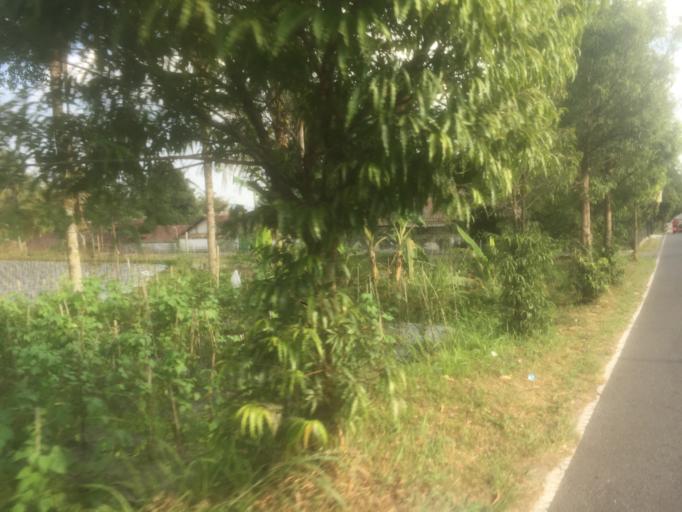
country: ID
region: Daerah Istimewa Yogyakarta
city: Sleman
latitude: -7.6434
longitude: 110.4248
